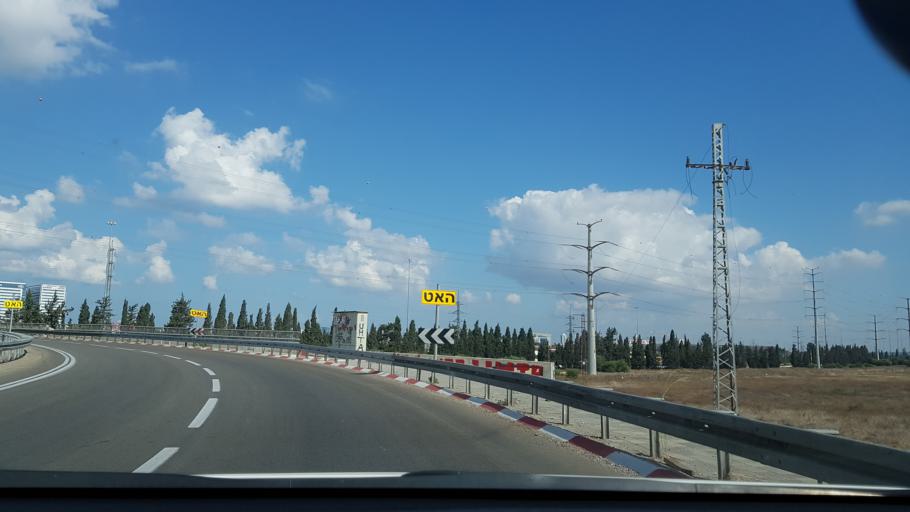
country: IL
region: Central District
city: Bet Dagan
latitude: 31.9985
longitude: 34.8064
